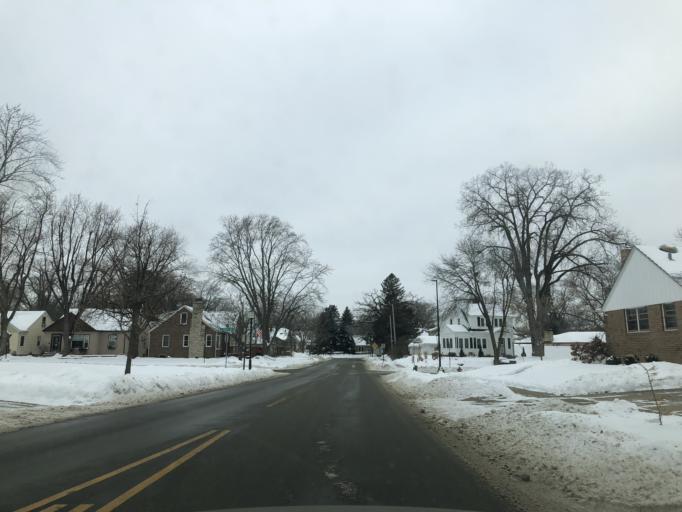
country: US
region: Minnesota
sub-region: Hennepin County
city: Robbinsdale
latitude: 45.0278
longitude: -93.3205
